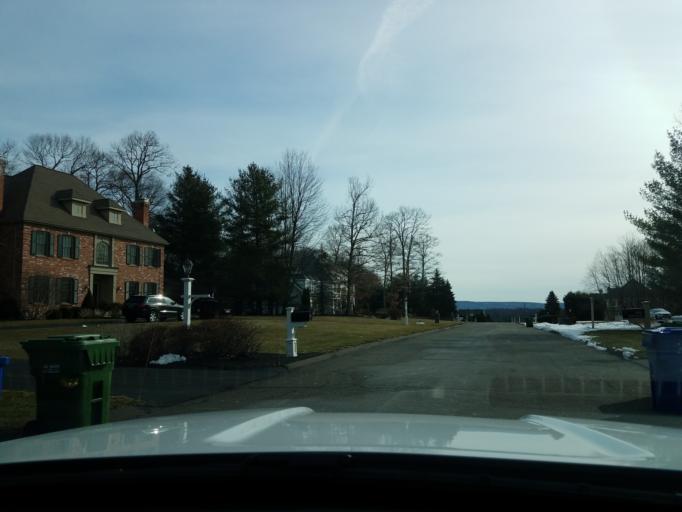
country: US
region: Connecticut
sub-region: Hartford County
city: Collinsville
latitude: 41.7928
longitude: -72.9028
